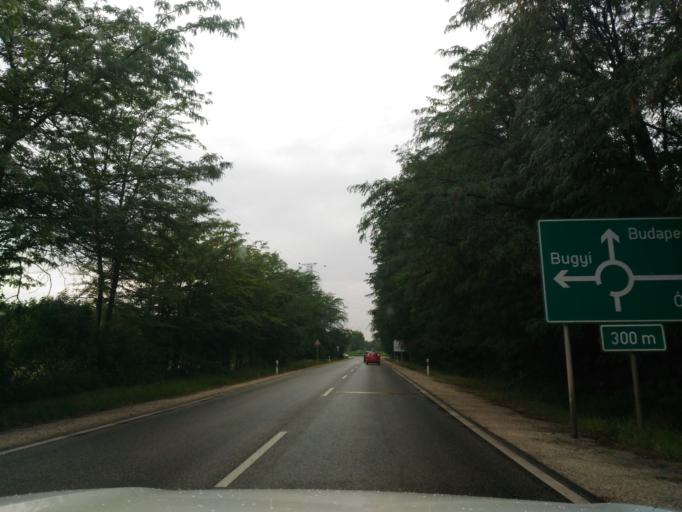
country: HU
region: Pest
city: Ocsa
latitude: 47.2570
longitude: 19.2228
